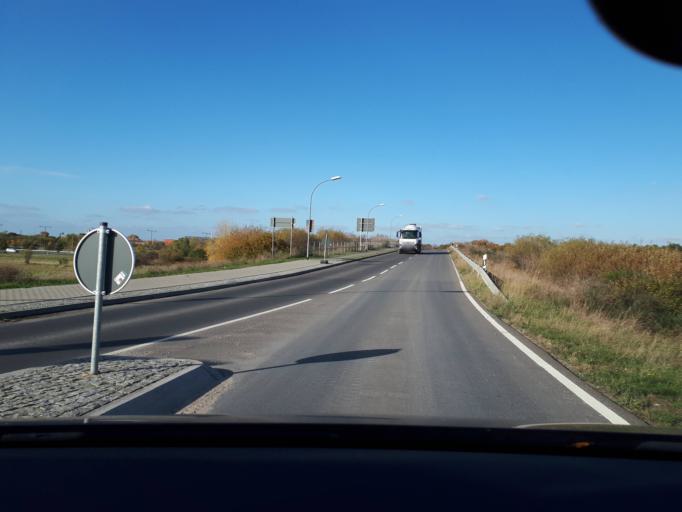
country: DE
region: Brandenburg
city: Schonefeld
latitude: 52.3694
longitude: 13.5408
